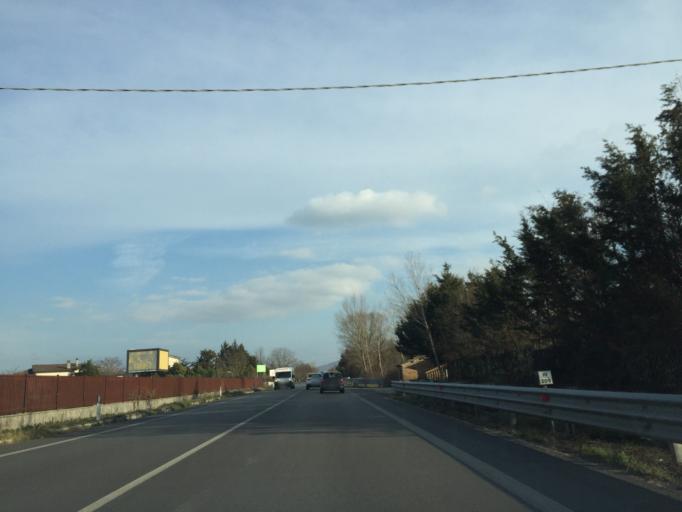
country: IT
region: Molise
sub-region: Provincia di Campobasso
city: San Polomatese
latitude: 41.4804
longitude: 14.4993
